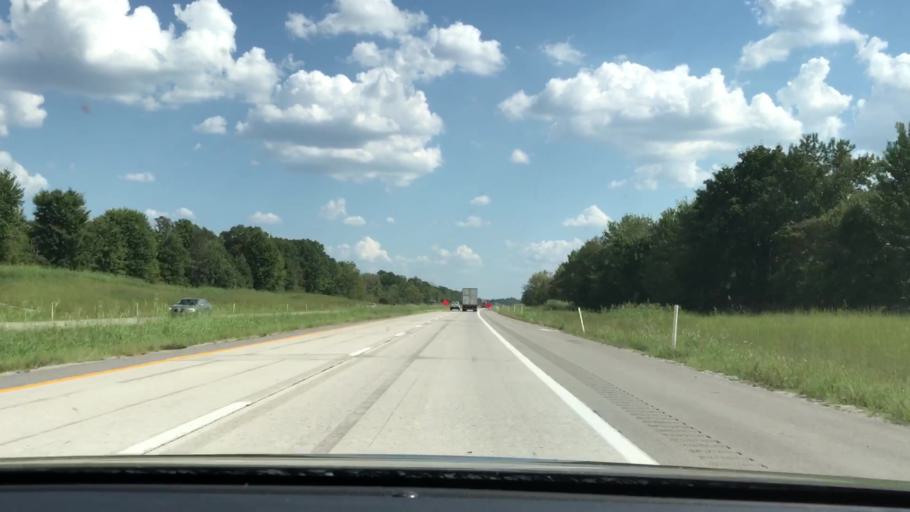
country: US
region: Kentucky
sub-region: Ohio County
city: Oak Grove
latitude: 37.3447
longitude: -86.7747
